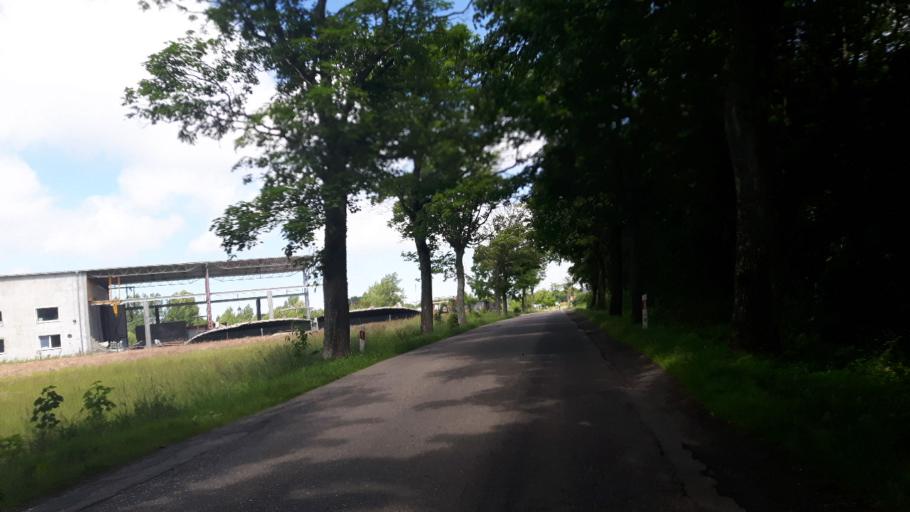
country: PL
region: Pomeranian Voivodeship
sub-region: Powiat slupski
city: Ustka
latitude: 54.5329
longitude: 16.8183
